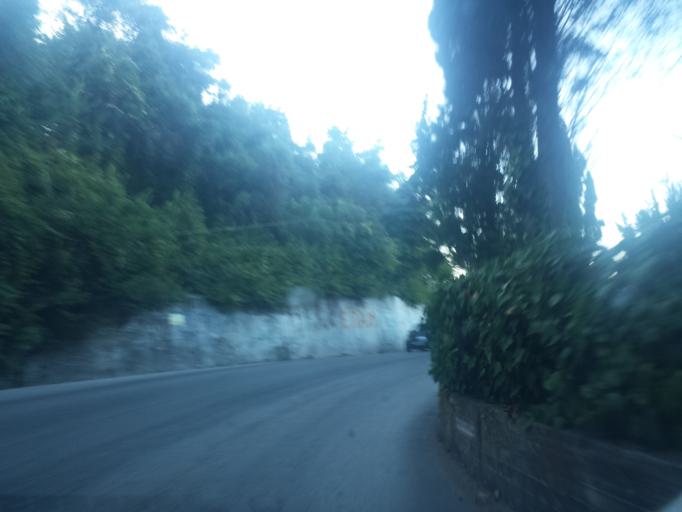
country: GR
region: Ionian Islands
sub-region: Nomos Kerkyras
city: Perama
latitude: 39.5564
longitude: 19.9115
